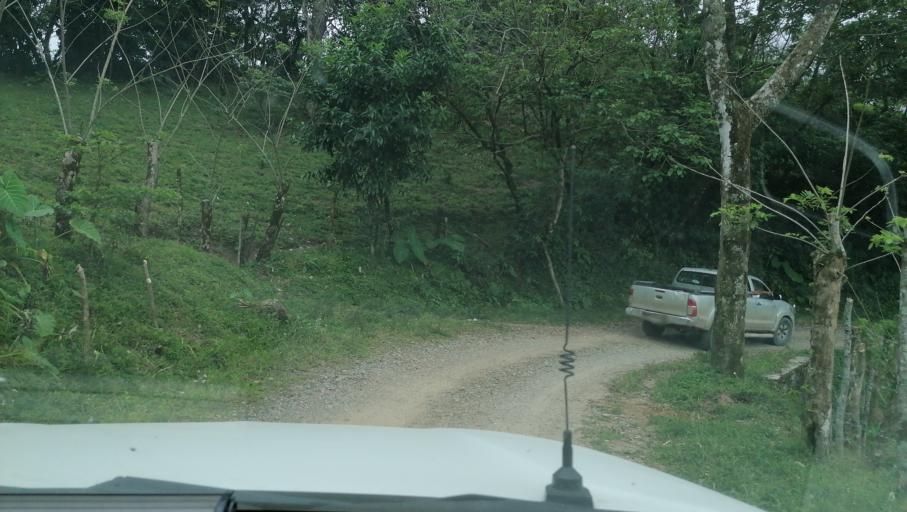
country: MX
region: Chiapas
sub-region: Francisco Leon
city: San Miguel la Sardina
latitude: 17.3322
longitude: -93.3102
